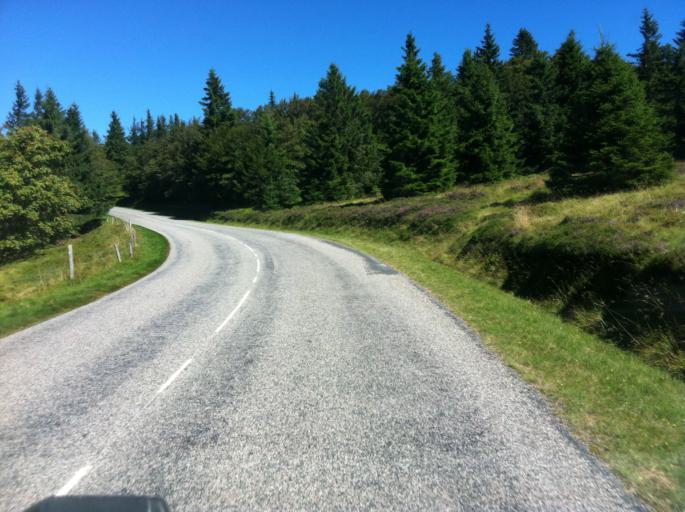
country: FR
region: Alsace
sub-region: Departement du Haut-Rhin
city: Soultzeren
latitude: 48.0864
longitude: 7.0475
